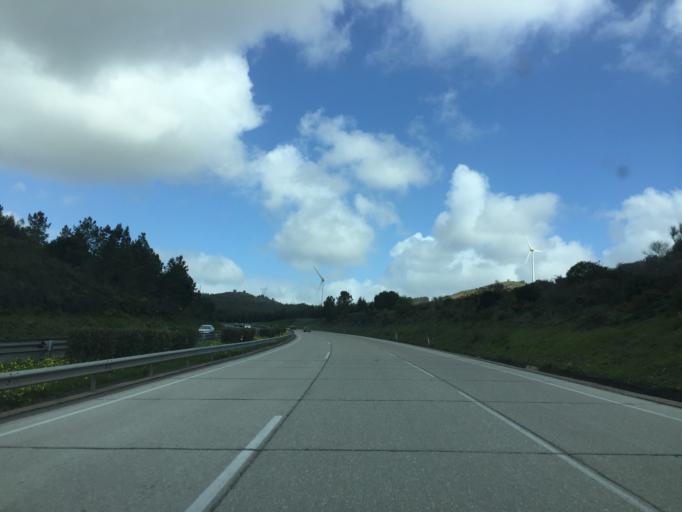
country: PT
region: Lisbon
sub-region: Sobral de Monte Agraco
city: Sobral de Monte Agraco
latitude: 39.0095
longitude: -9.2119
